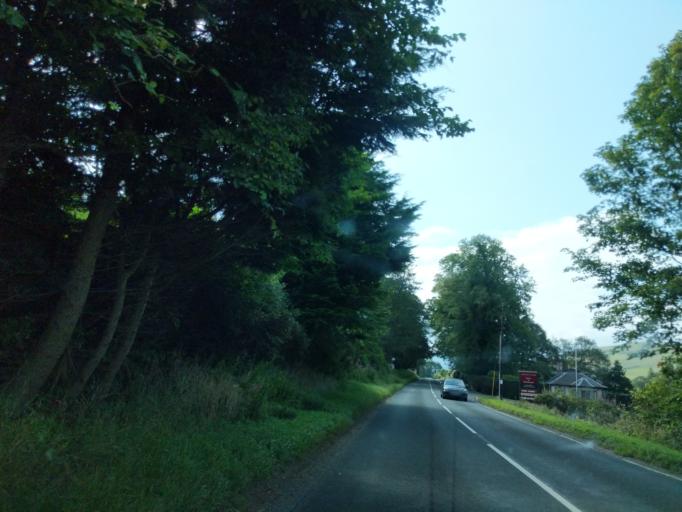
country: GB
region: Scotland
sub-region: The Scottish Borders
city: Peebles
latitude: 55.6889
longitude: -3.2122
